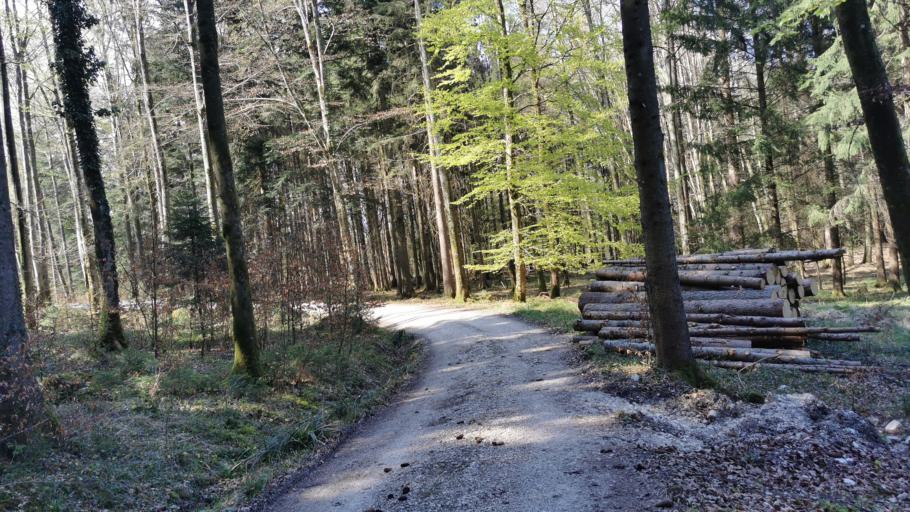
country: AT
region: Salzburg
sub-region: Politischer Bezirk Salzburg-Umgebung
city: Grodig
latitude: 47.7452
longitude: 12.9749
